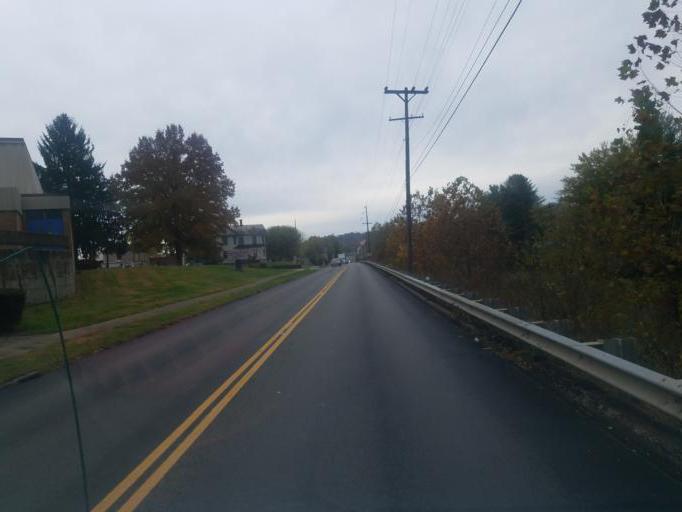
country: US
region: Ohio
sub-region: Washington County
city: Devola
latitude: 39.5312
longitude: -81.5095
